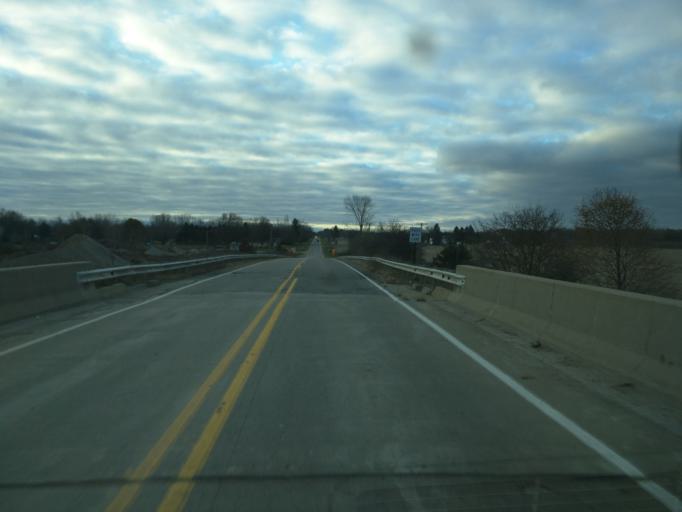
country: US
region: Michigan
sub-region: Eaton County
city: Dimondale
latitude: 42.6656
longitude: -84.6030
